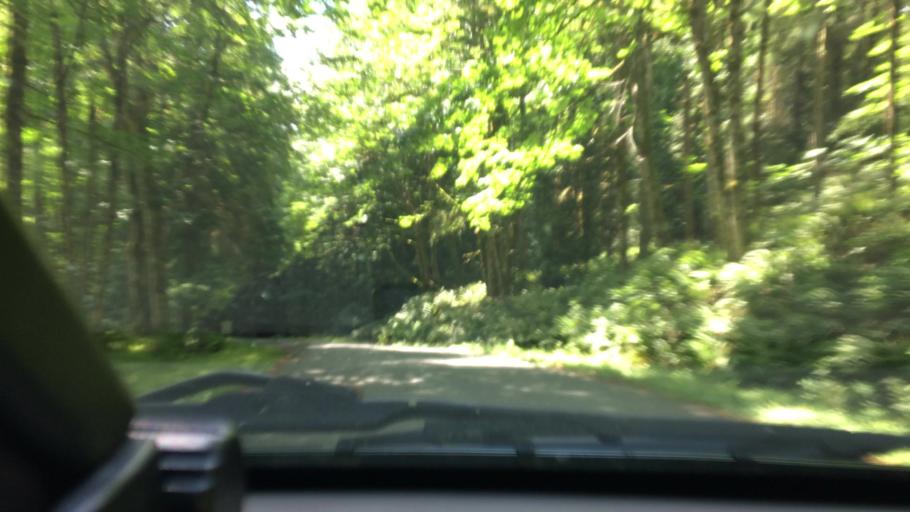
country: US
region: Washington
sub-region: Whatcom County
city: Geneva
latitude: 48.7651
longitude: -122.3698
